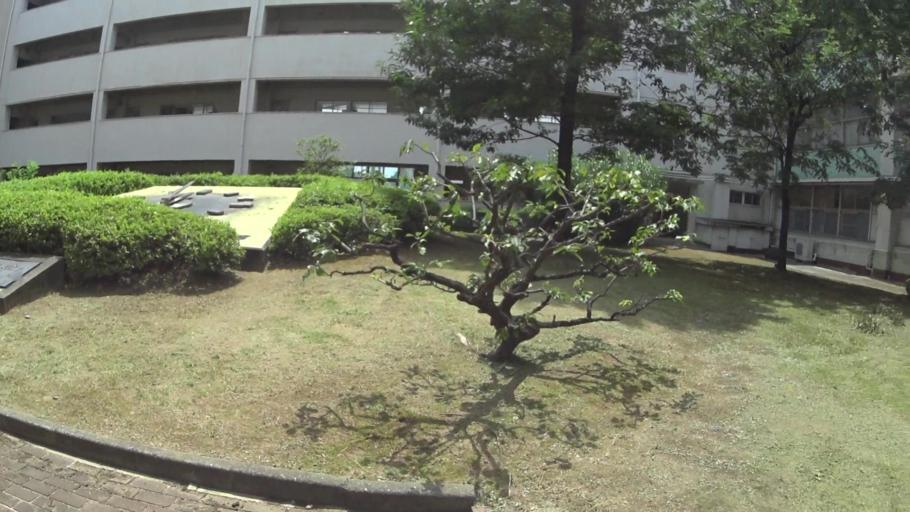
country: JP
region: Osaka
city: Yao
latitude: 34.6501
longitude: 135.5877
